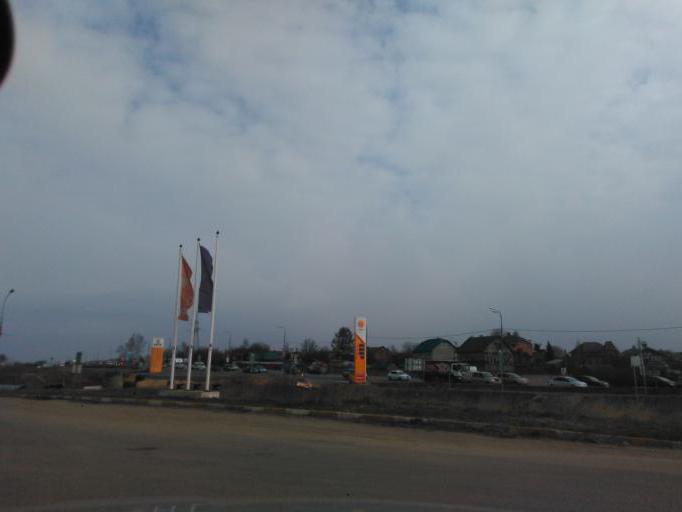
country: RU
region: Moskovskaya
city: Yermolino
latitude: 56.1402
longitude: 37.4932
